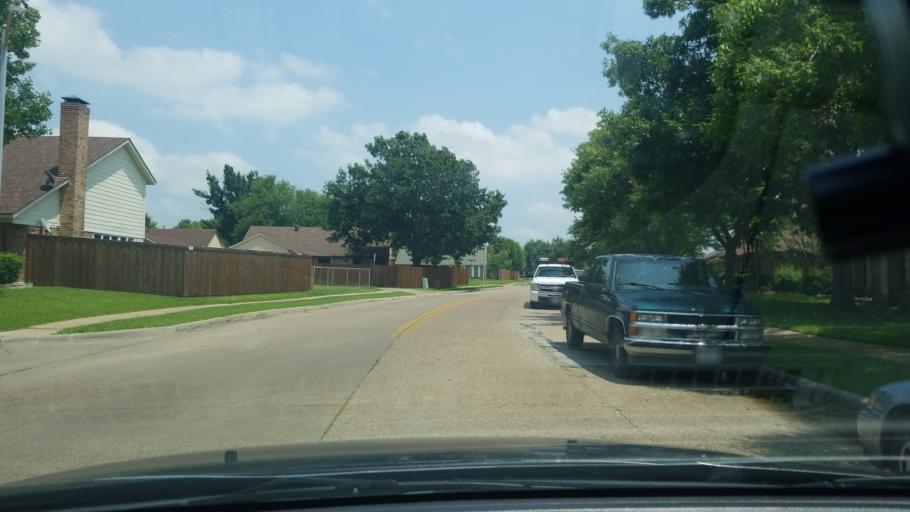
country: US
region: Texas
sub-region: Dallas County
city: Mesquite
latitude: 32.8065
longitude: -96.6450
